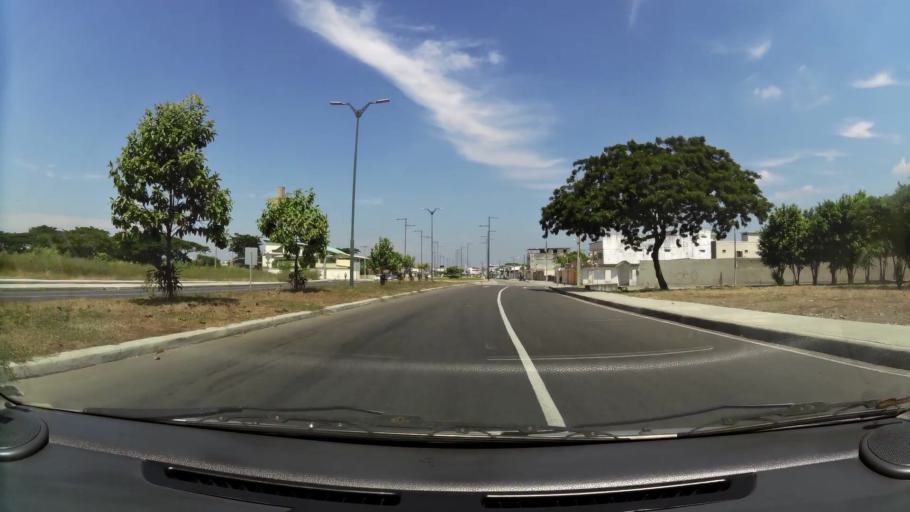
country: EC
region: Guayas
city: Eloy Alfaro
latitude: -2.1071
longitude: -79.8991
